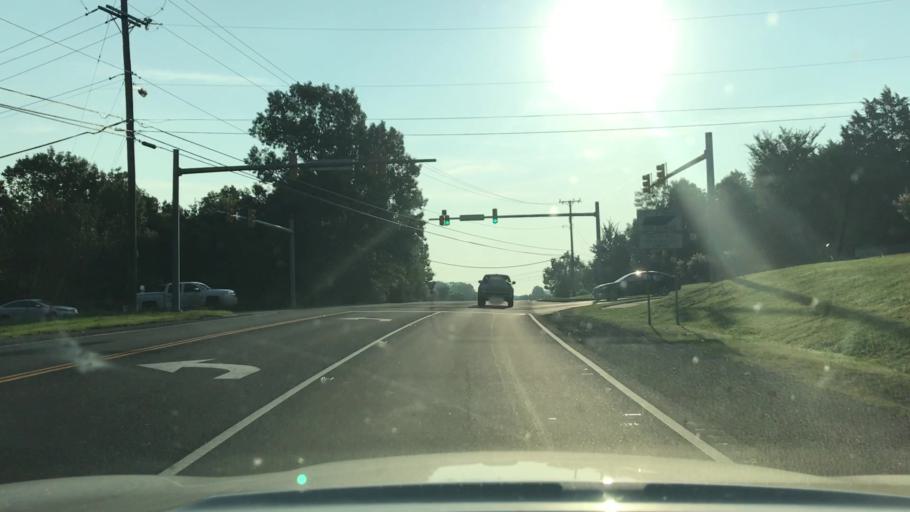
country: US
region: Tennessee
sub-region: Rutherford County
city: La Vergne
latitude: 36.0683
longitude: -86.5857
